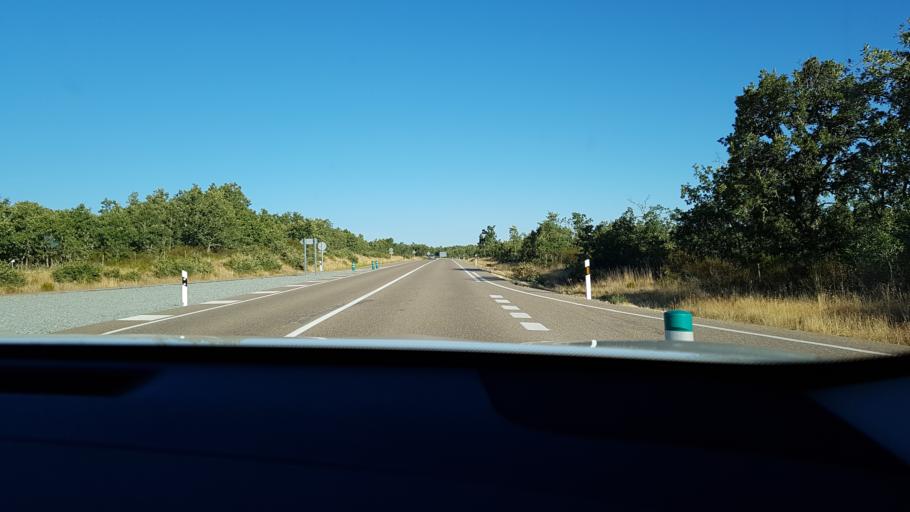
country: ES
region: Castille and Leon
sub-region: Provincia de Zamora
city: Samir de los Canos
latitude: 41.6692
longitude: -6.2267
